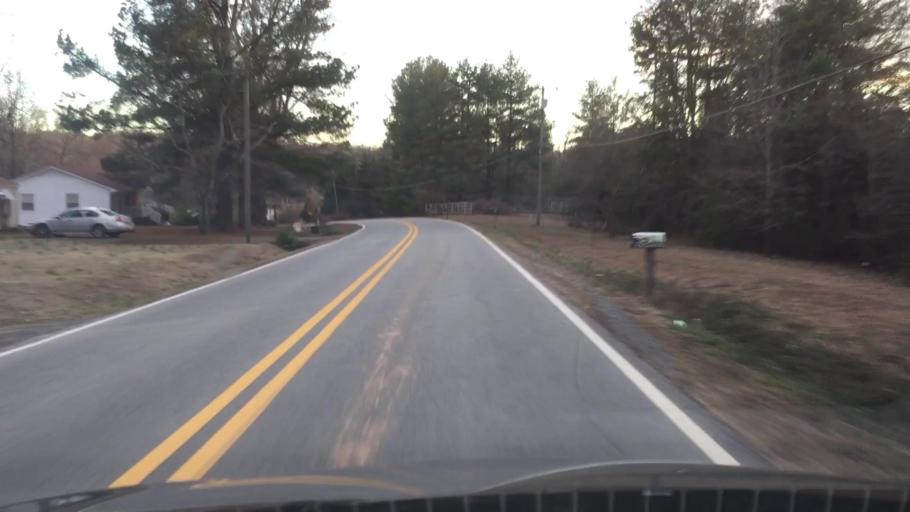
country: US
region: North Carolina
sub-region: Rockingham County
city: Reidsville
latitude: 36.4016
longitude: -79.6588
